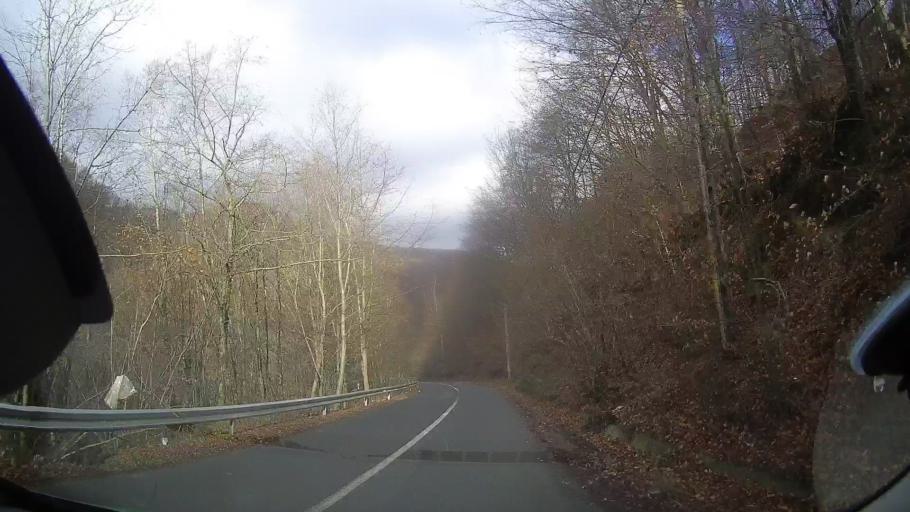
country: RO
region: Cluj
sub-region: Comuna Valea Ierii
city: Valea Ierii
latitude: 46.6866
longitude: 23.3067
